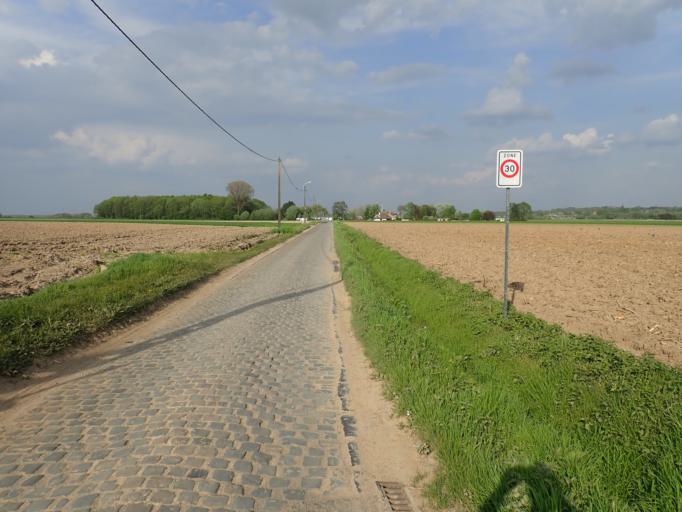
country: BE
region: Flanders
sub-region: Provincie Vlaams-Brabant
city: Wemmel
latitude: 50.9410
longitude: 4.2768
